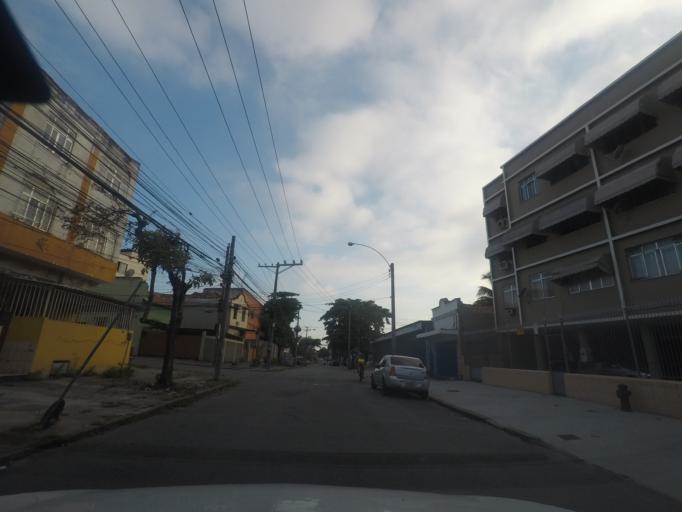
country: BR
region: Rio de Janeiro
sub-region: Duque De Caxias
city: Duque de Caxias
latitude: -22.8353
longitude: -43.2793
